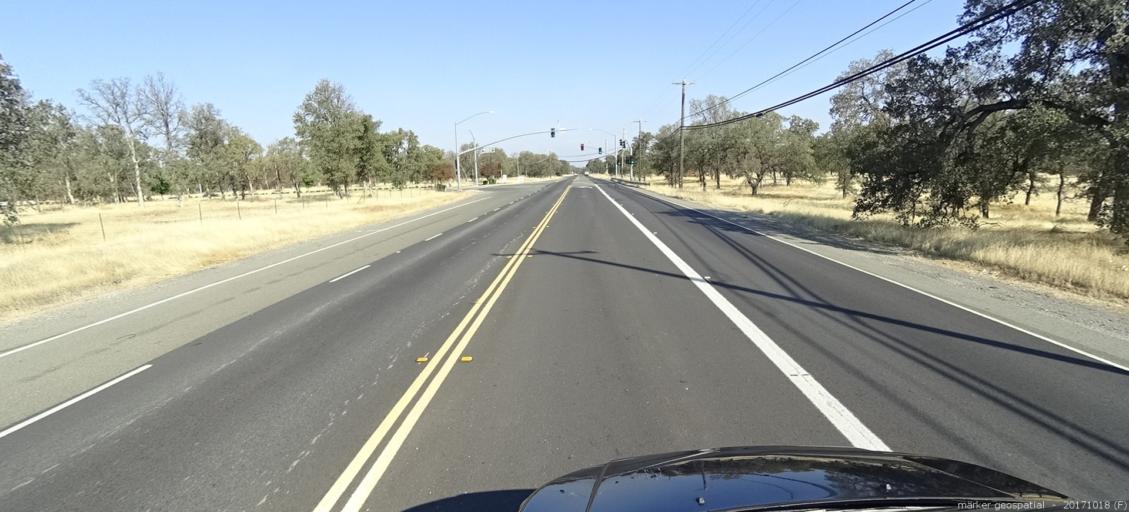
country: US
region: California
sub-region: Shasta County
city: Palo Cedro
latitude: 40.5509
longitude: -122.3028
